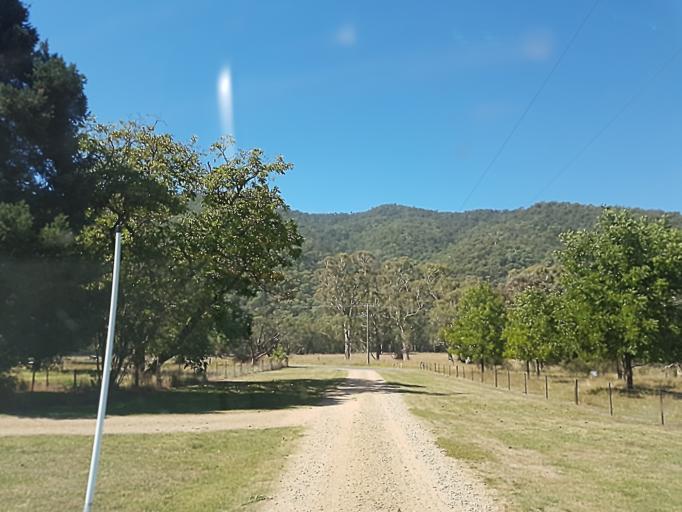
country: AU
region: Victoria
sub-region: Alpine
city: Mount Beauty
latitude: -36.8208
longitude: 147.0644
